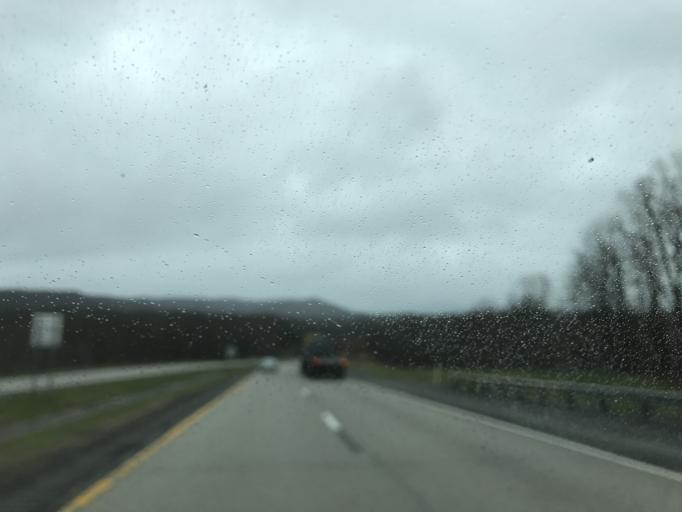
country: US
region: West Virginia
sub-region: Summers County
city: Hinton
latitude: 37.7753
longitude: -80.9777
